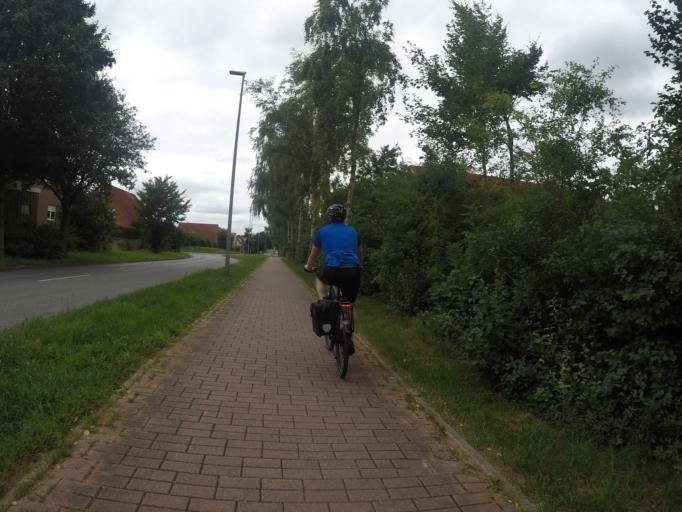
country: DE
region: Lower Saxony
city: Hammah
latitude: 53.5987
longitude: 9.4154
